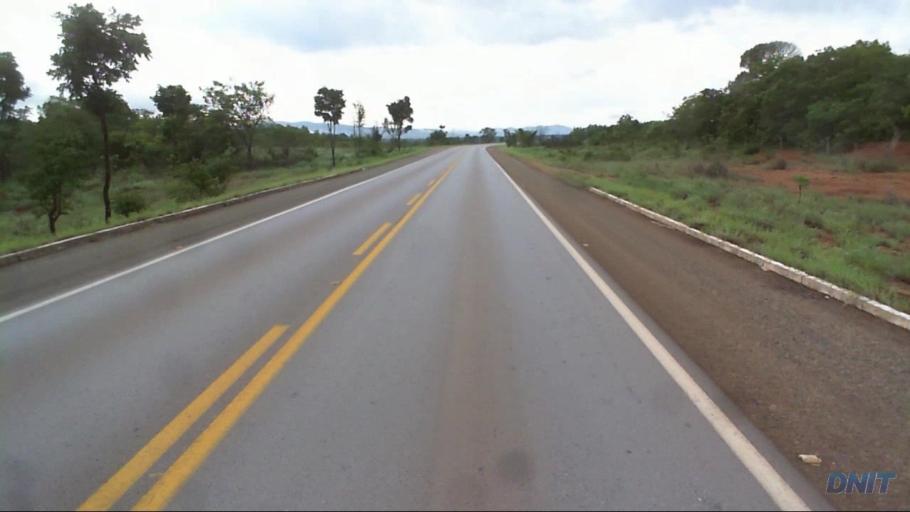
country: BR
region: Goias
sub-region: Uruacu
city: Uruacu
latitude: -14.7363
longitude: -49.0863
